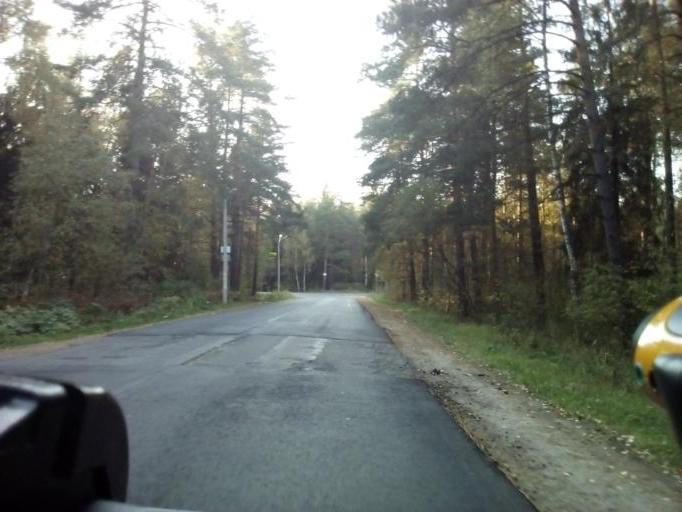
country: RU
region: Moskovskaya
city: Ramenskoye
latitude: 55.6138
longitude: 38.2796
